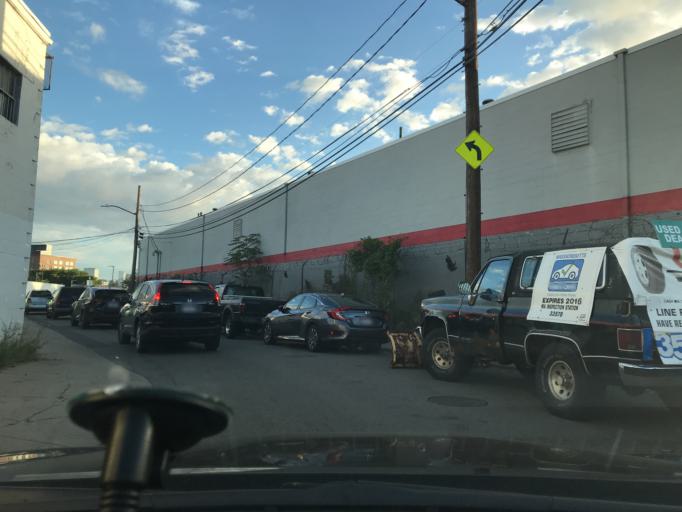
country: US
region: Massachusetts
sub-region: Suffolk County
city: South Boston
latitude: 42.3251
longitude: -71.0678
